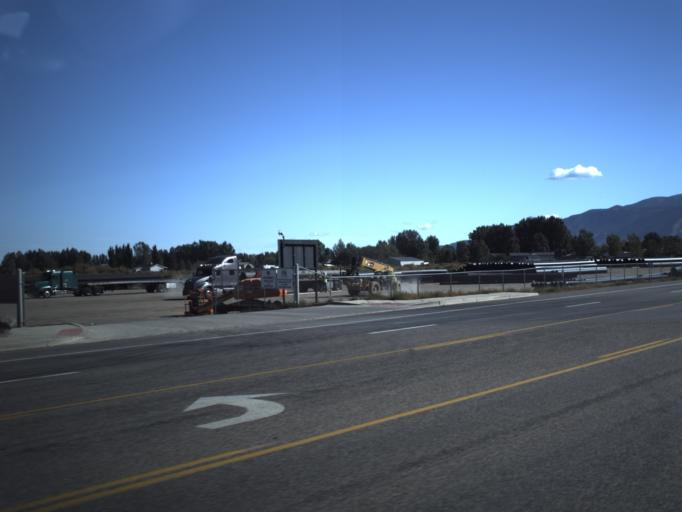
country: US
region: Utah
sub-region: Iron County
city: Cedar City
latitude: 37.6849
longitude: -113.1464
